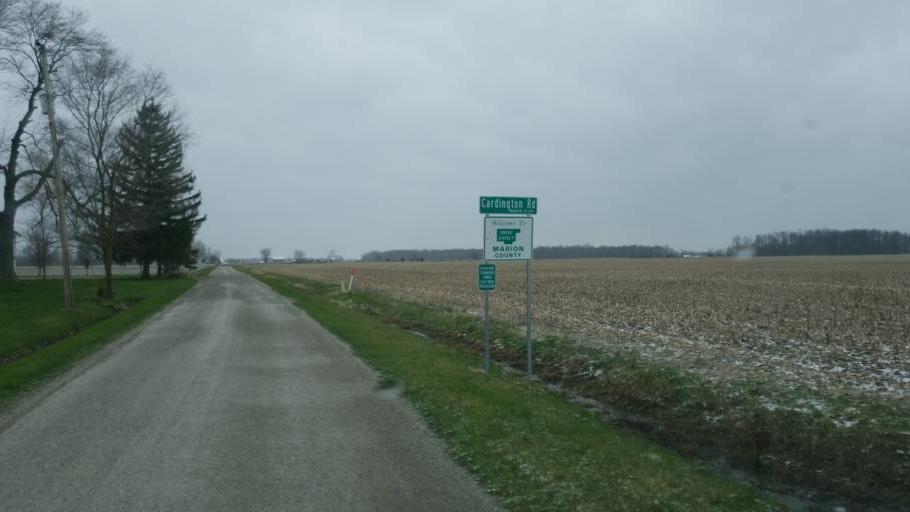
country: US
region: Ohio
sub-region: Morrow County
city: Cardington
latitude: 40.5144
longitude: -82.9581
